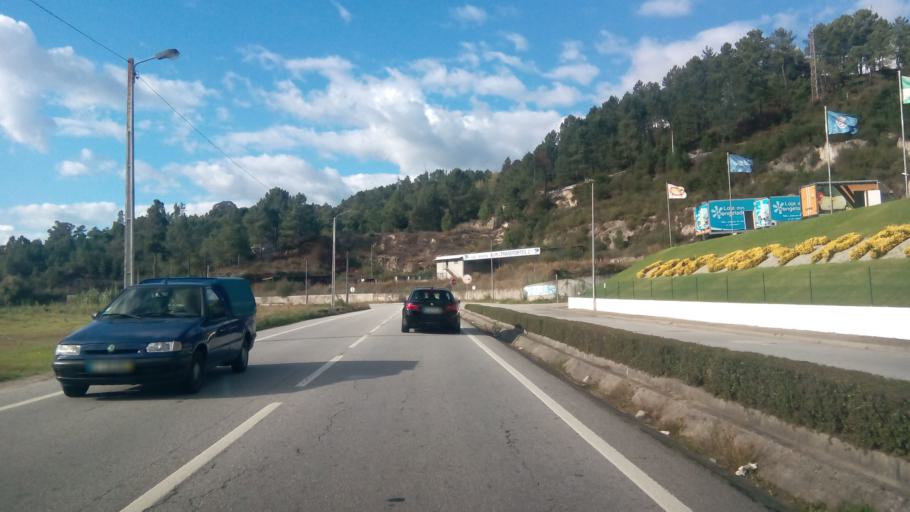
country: PT
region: Porto
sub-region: Amarante
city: Amarante
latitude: 41.2525
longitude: -8.0392
